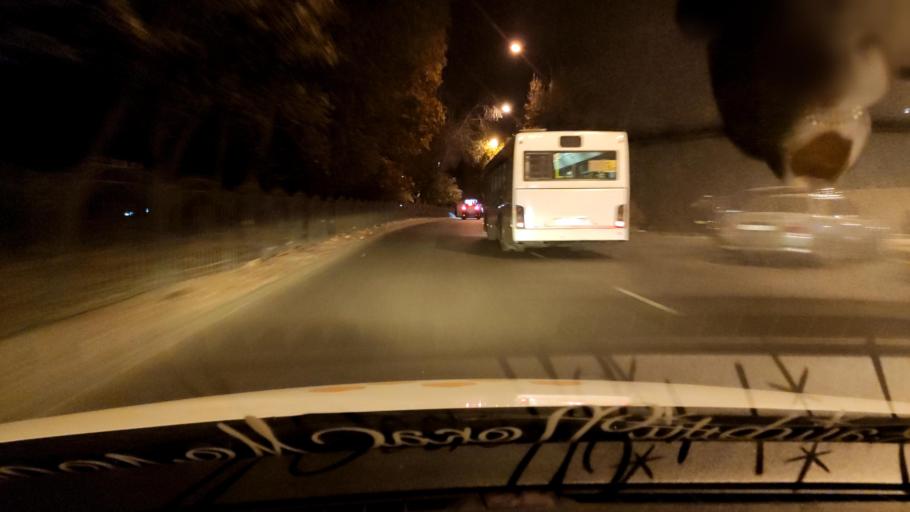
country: RU
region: Voronezj
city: Voronezh
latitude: 51.7097
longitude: 39.2298
